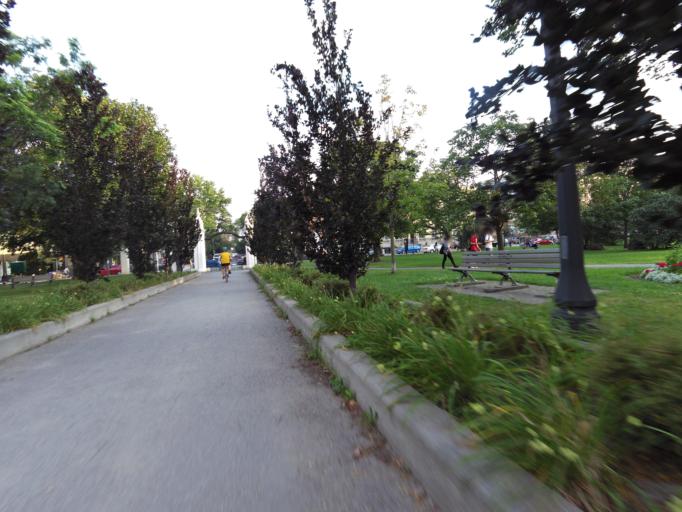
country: CA
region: Ontario
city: Toronto
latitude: 43.6458
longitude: -79.4134
